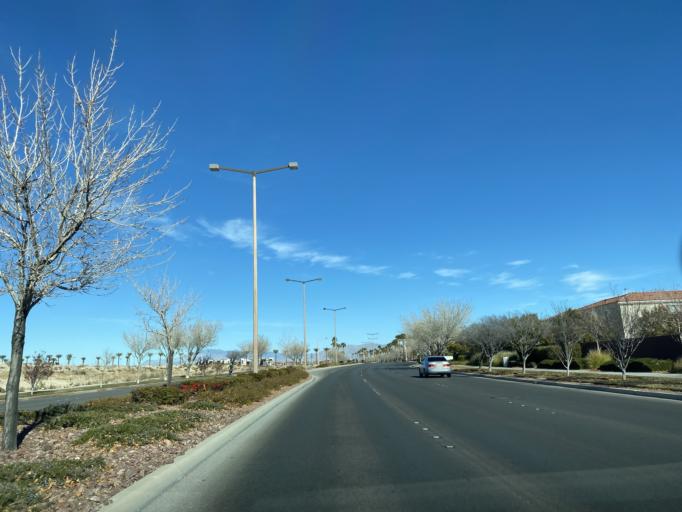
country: US
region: Nevada
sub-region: Clark County
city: Summerlin South
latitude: 36.1478
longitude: -115.3259
